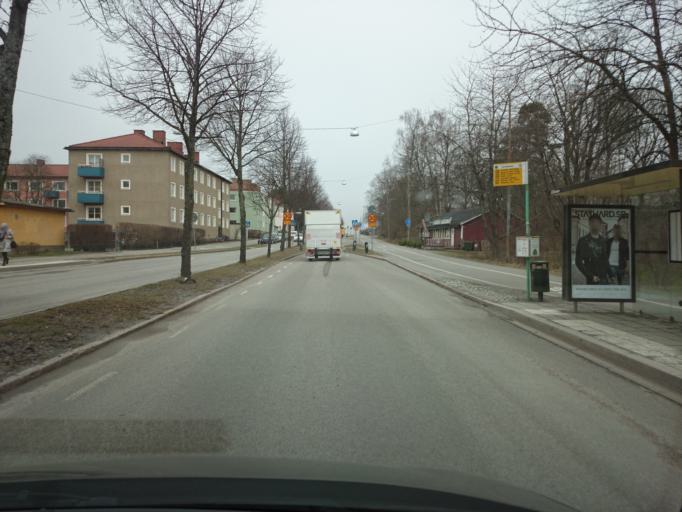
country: SE
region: Uppsala
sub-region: Uppsala Kommun
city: Uppsala
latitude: 59.8753
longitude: 17.6247
